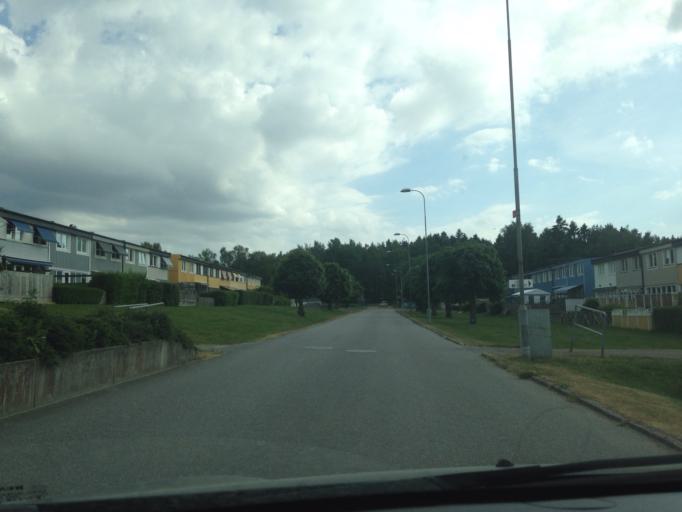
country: SE
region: Vaestra Goetaland
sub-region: Goteborg
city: Majorna
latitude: 57.7478
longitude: 11.9189
